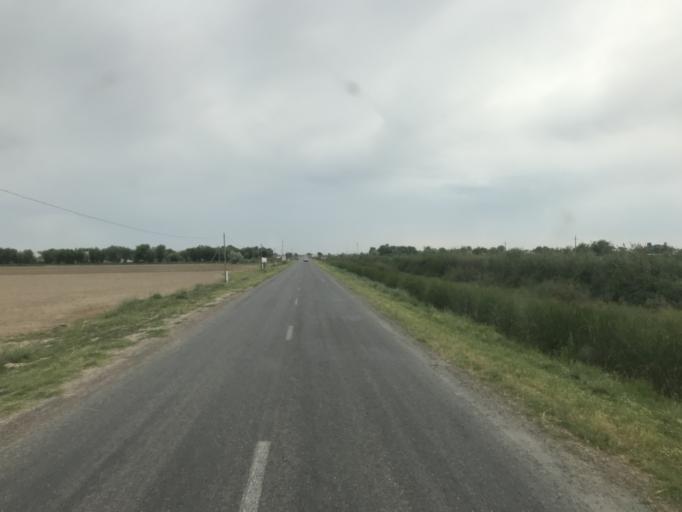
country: KZ
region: Ongtustik Qazaqstan
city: Asykata
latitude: 40.9176
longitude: 68.3975
